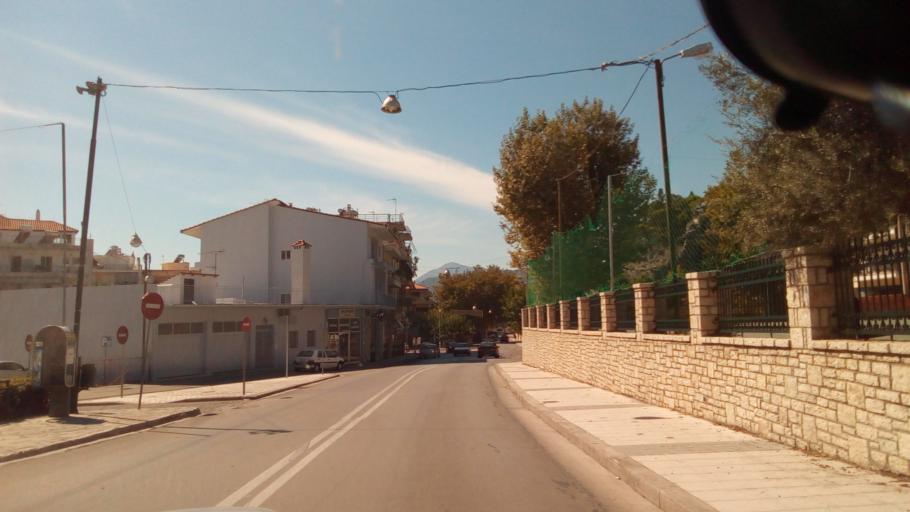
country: GR
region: West Greece
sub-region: Nomos Aitolias kai Akarnanias
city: Nafpaktos
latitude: 38.3944
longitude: 21.8404
